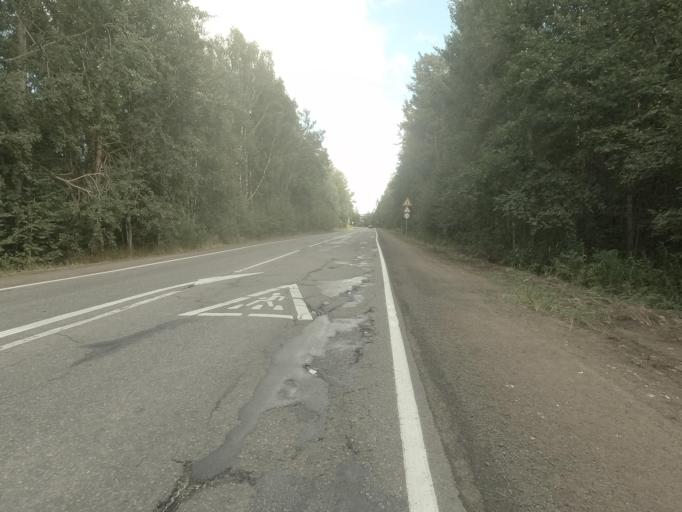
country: RU
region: Leningrad
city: Shcheglovo
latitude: 60.0195
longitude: 30.7399
